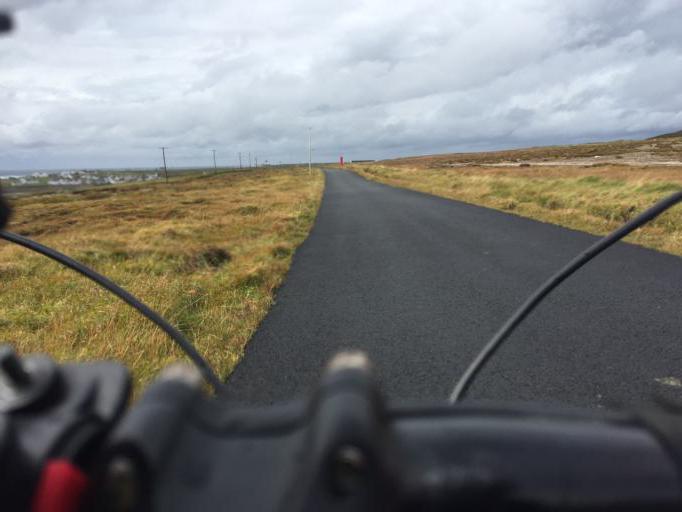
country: IE
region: Ulster
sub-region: County Donegal
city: Derrybeg
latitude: 55.2618
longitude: -8.2146
